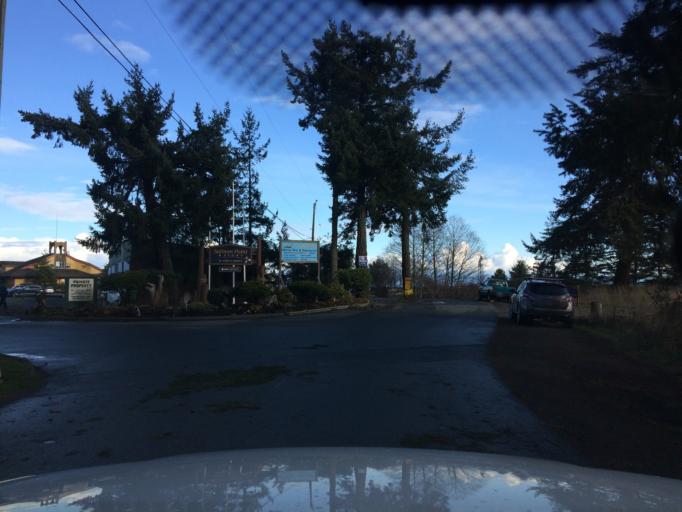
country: CA
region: British Columbia
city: Campbell River
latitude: 49.8884
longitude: -125.1270
